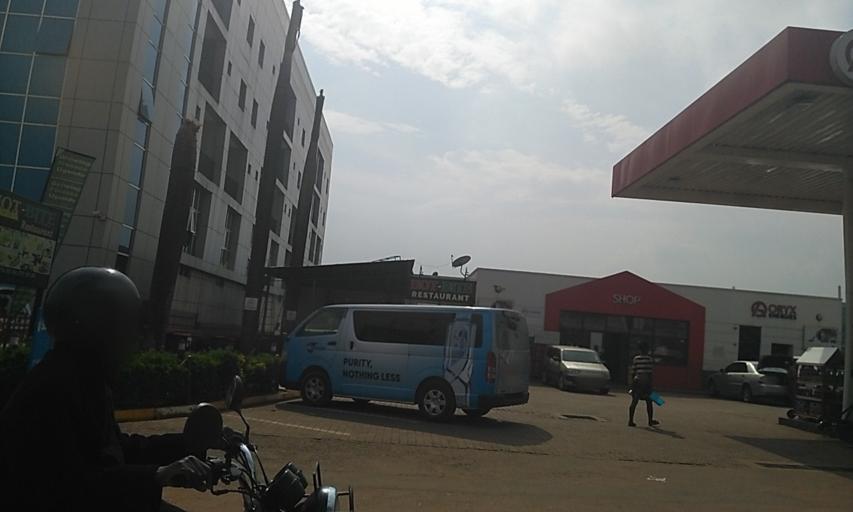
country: UG
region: Central Region
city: Kampala Central Division
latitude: 0.3080
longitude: 32.5629
